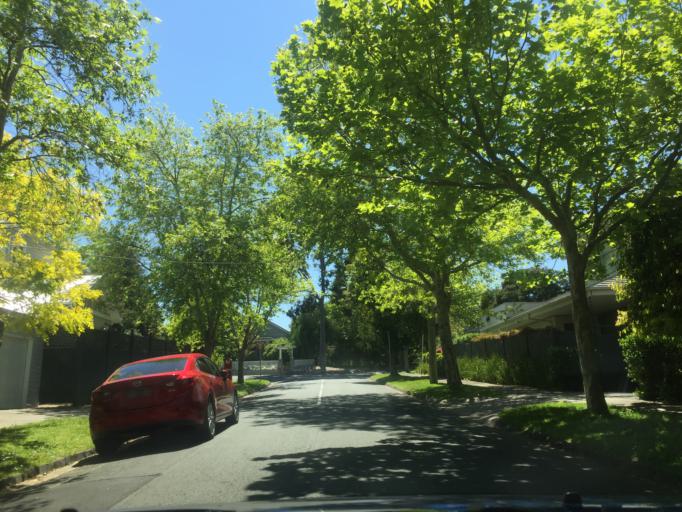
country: AU
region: Victoria
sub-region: Whitehorse
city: Surrey Hills
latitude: -37.8228
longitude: 145.0936
